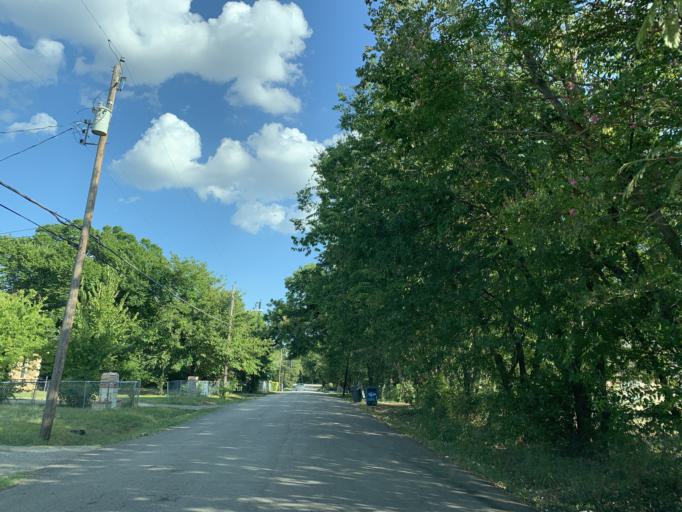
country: US
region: Texas
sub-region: Dallas County
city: Hutchins
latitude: 32.6942
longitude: -96.7783
